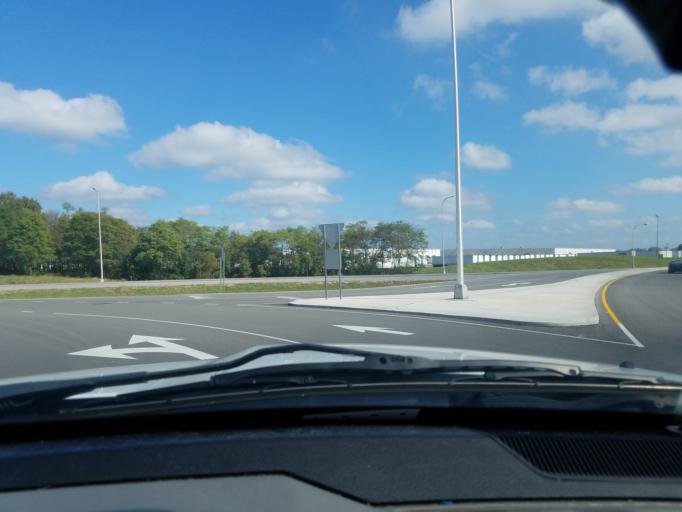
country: US
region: Kentucky
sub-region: Scott County
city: Georgetown
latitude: 38.2478
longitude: -84.5351
